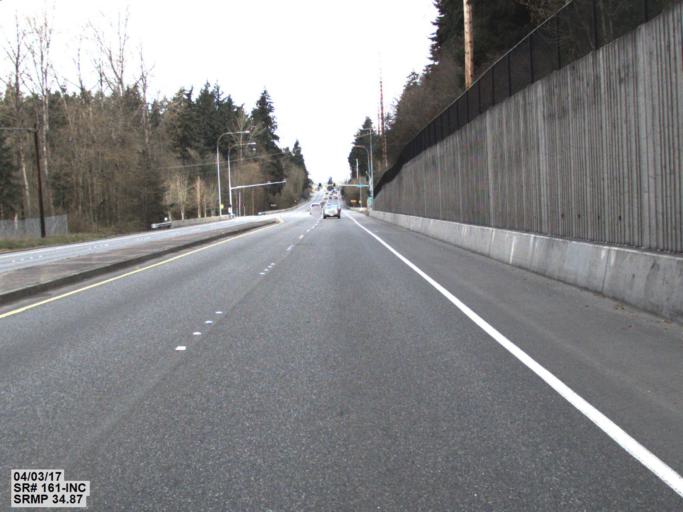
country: US
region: Washington
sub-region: King County
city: Lakeland South
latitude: 47.2708
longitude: -122.3045
